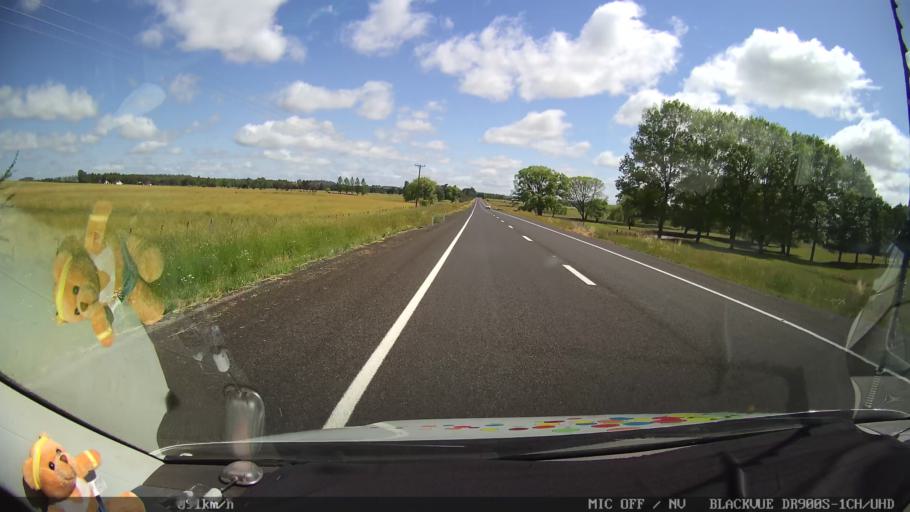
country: AU
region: New South Wales
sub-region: Glen Innes Severn
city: Glen Innes
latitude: -29.8319
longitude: 151.7377
